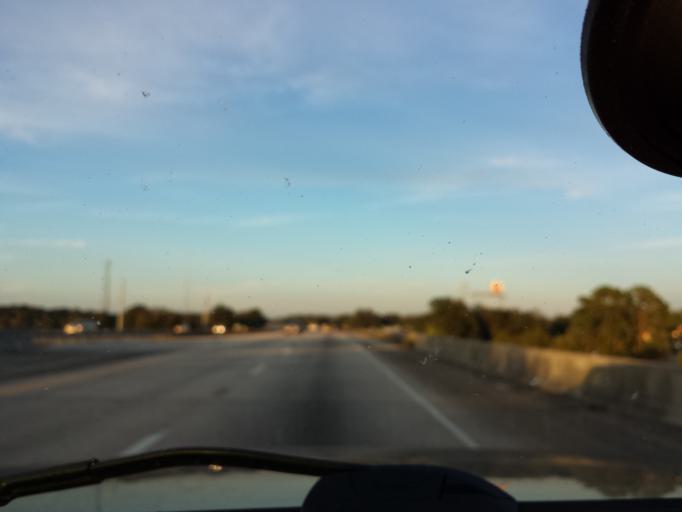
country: US
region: Florida
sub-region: Sumter County
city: Bushnell
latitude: 28.6685
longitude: -82.1426
